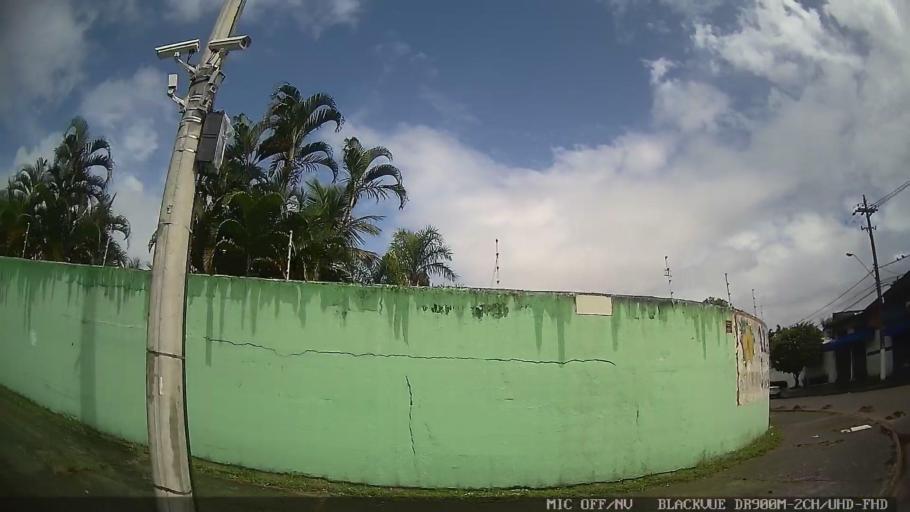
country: BR
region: Sao Paulo
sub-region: Itanhaem
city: Itanhaem
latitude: -24.1808
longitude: -46.8191
